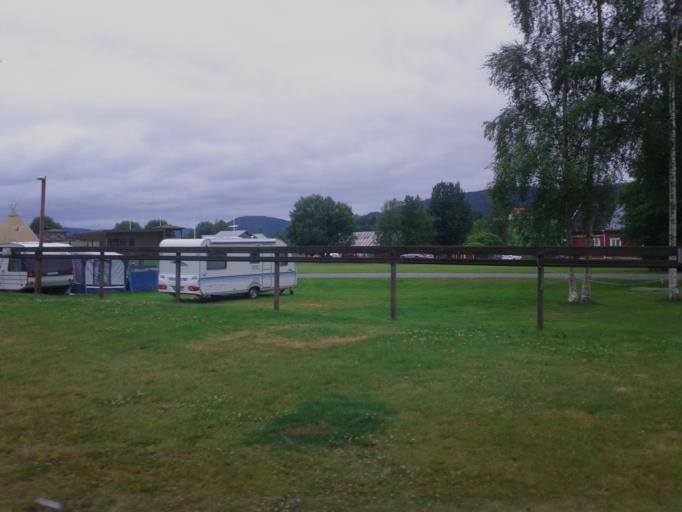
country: SE
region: Vaesternorrland
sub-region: Kramfors Kommun
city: Nordingra
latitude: 63.0656
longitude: 18.3373
